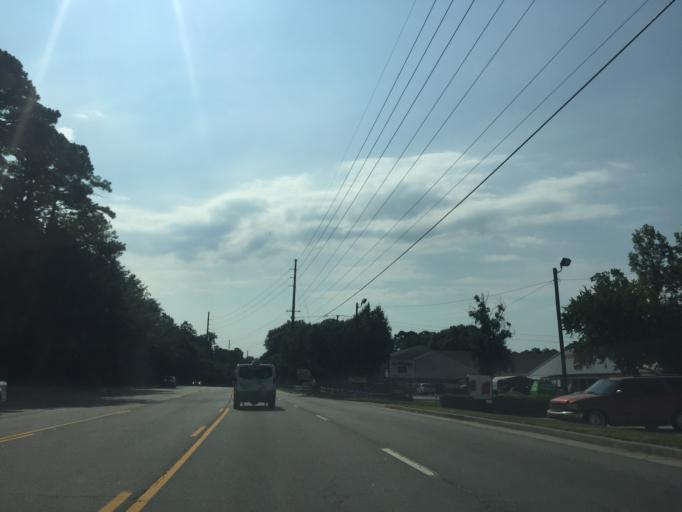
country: US
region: Georgia
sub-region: Chatham County
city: Isle of Hope
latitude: 31.9918
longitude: -81.0965
